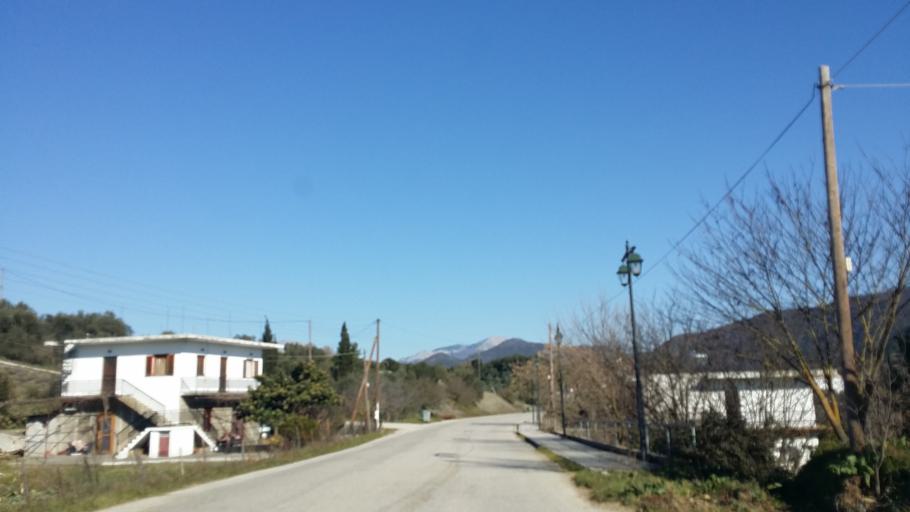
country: GR
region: West Greece
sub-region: Nomos Aitolias kai Akarnanias
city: Sardinia
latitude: 38.8566
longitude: 21.3360
